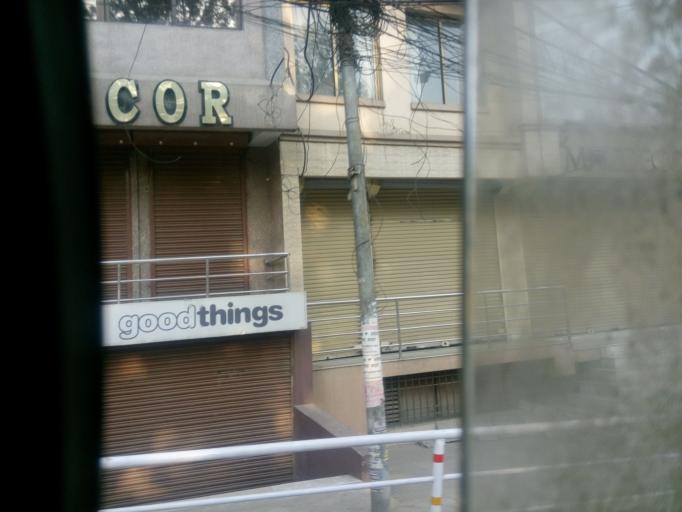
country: NP
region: Central Region
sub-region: Bagmati Zone
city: Patan
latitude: 27.6828
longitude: 85.3188
